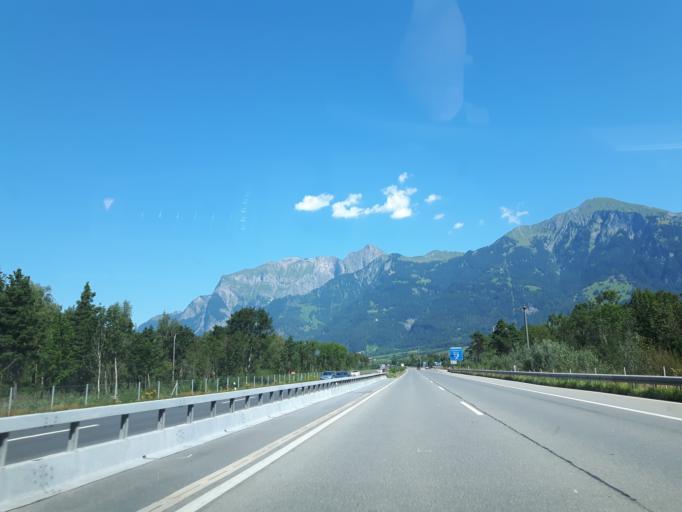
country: CH
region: Grisons
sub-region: Landquart District
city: Landquart
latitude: 46.9611
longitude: 9.5498
